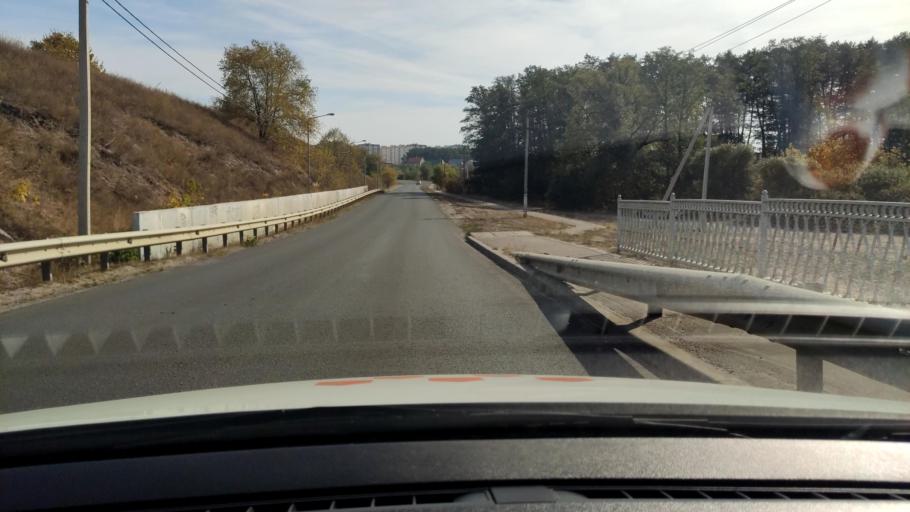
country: RU
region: Voronezj
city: Pridonskoy
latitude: 51.6646
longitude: 39.0887
